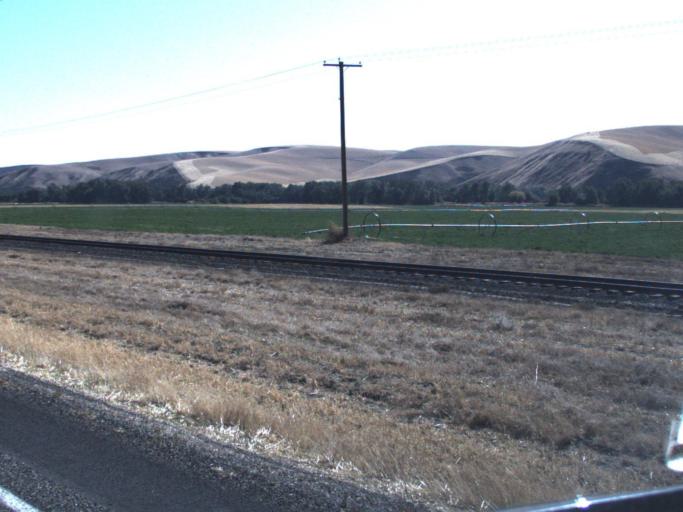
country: US
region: Washington
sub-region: Walla Walla County
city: Waitsburg
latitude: 46.2949
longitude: -118.2703
